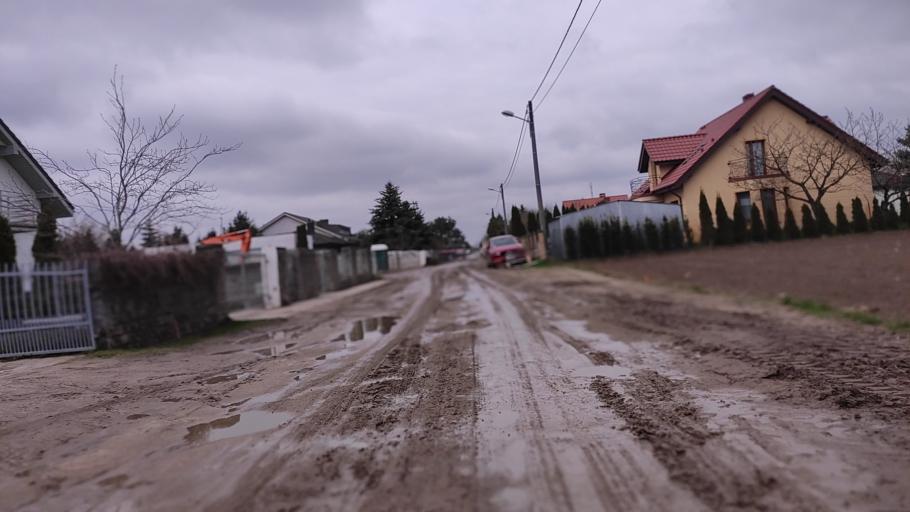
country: PL
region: Greater Poland Voivodeship
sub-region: Powiat poznanski
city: Kostrzyn
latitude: 52.4015
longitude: 17.1713
